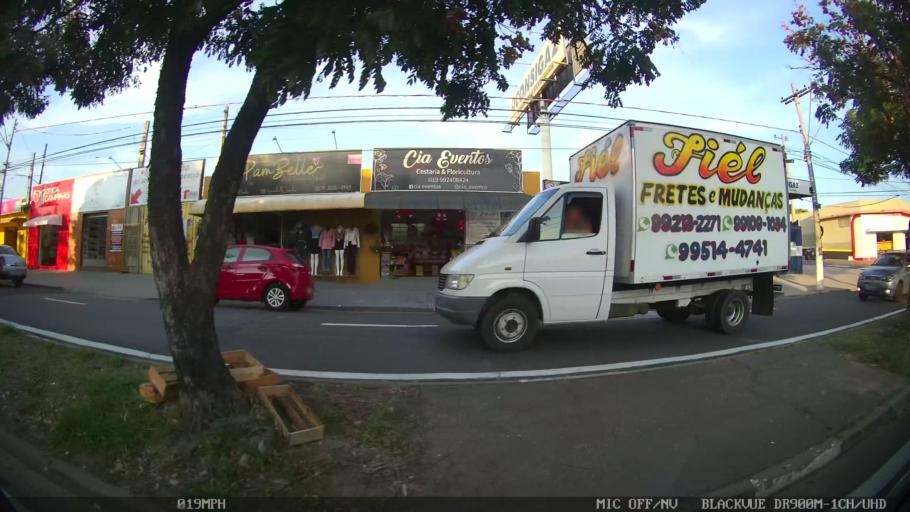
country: BR
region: Sao Paulo
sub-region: Campinas
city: Campinas
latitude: -22.9736
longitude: -47.1283
